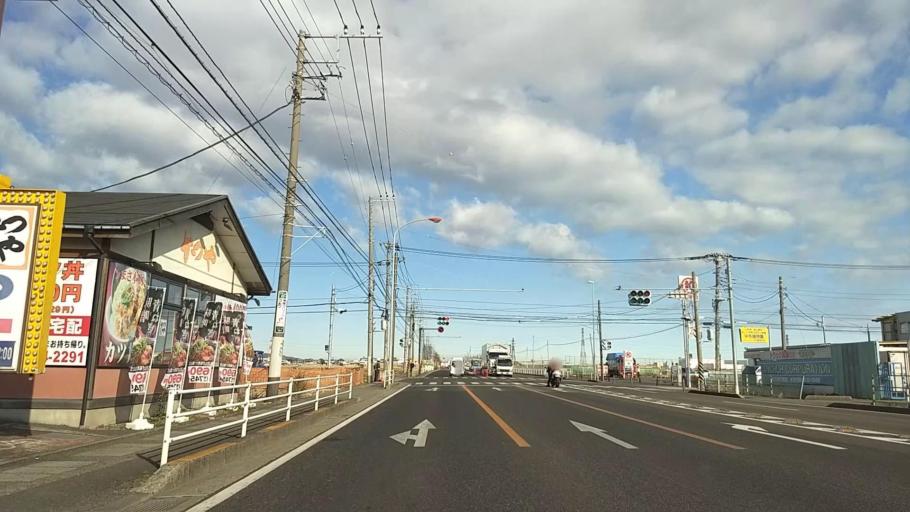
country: JP
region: Kanagawa
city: Atsugi
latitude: 35.3882
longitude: 139.3615
